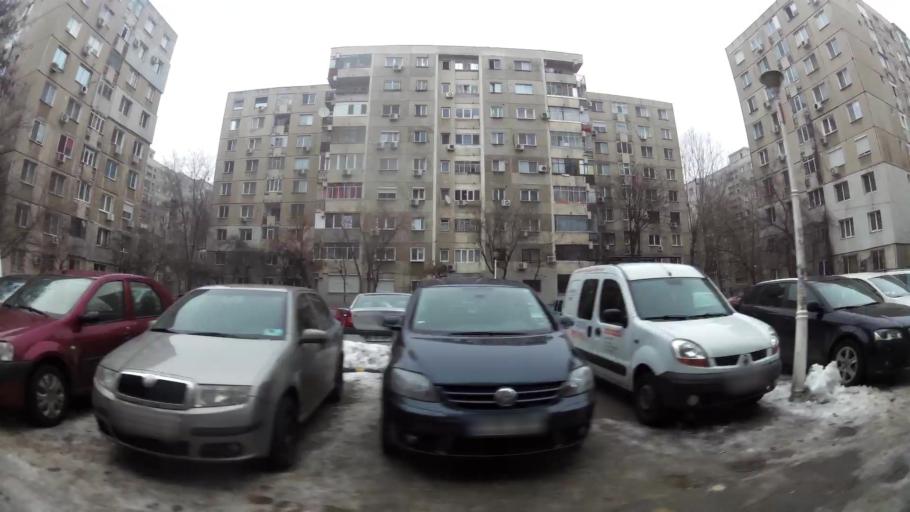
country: RO
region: Ilfov
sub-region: Comuna Chiajna
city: Rosu
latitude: 44.4580
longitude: 26.0483
